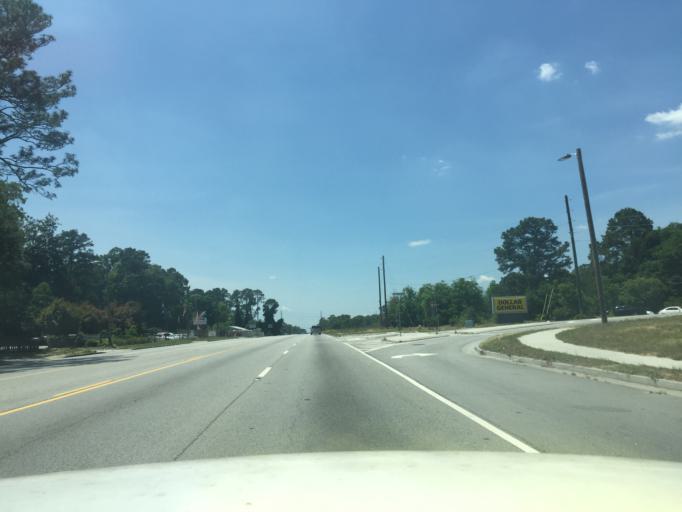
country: US
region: Georgia
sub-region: Chatham County
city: Garden City
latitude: 32.0456
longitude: -81.1770
